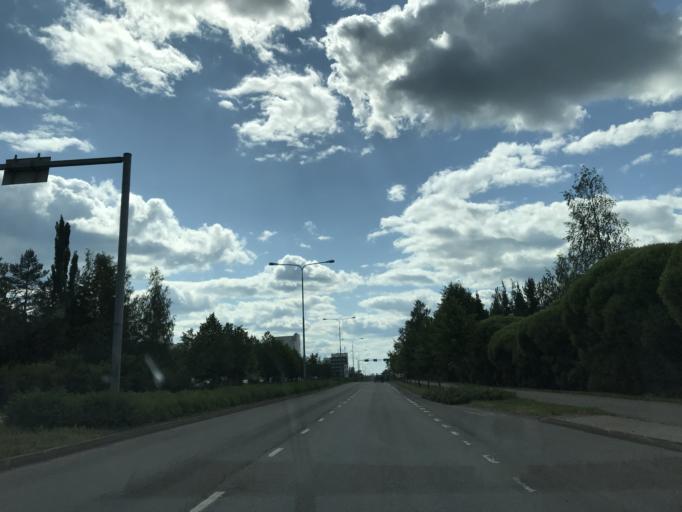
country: FI
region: Uusimaa
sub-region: Helsinki
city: Maentsaelae
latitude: 60.6393
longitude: 25.3215
